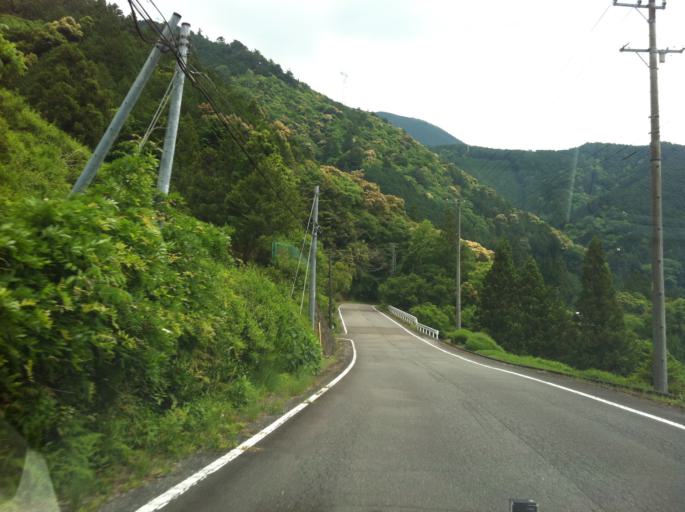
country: JP
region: Shizuoka
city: Shizuoka-shi
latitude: 35.1659
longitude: 138.3238
